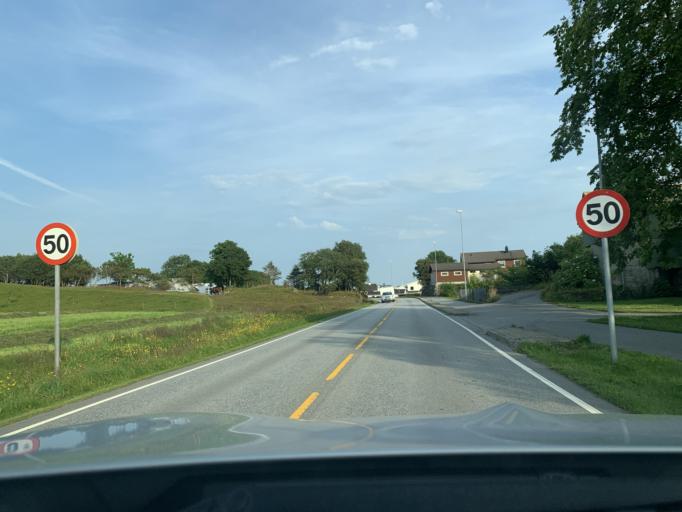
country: NO
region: Rogaland
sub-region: Time
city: Bryne
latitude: 58.7392
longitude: 5.6290
